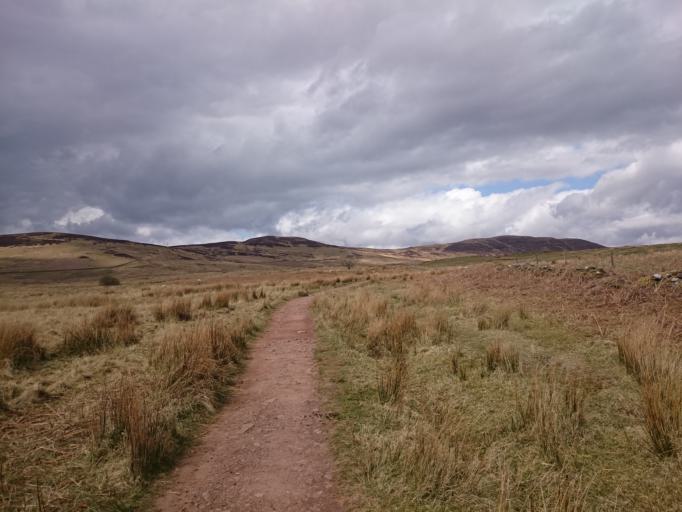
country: GB
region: Scotland
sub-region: West Dunbartonshire
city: Balloch
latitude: 56.0963
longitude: -4.4914
